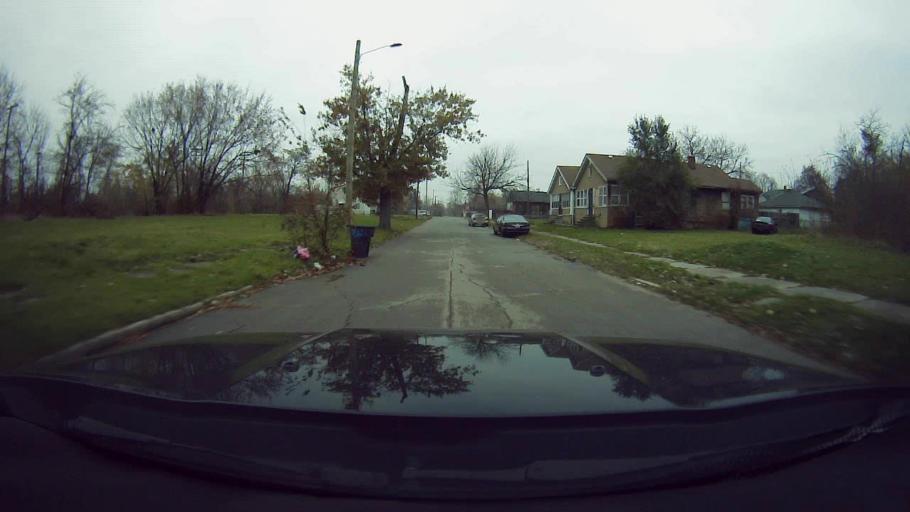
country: US
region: Michigan
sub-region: Wayne County
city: Highland Park
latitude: 42.4202
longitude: -83.0989
